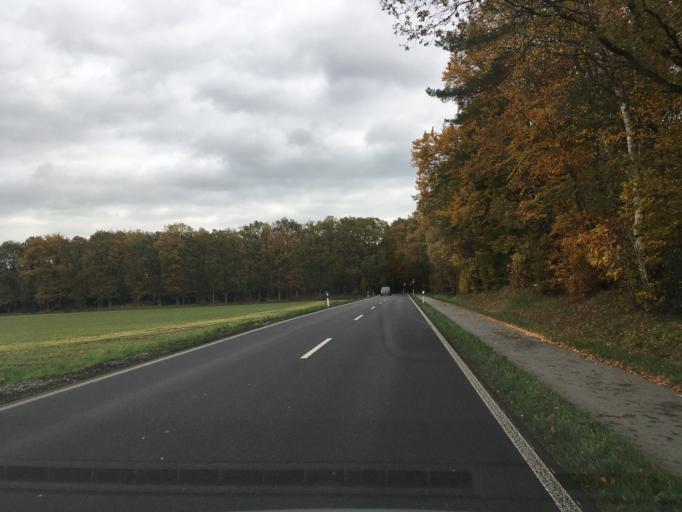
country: DE
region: North Rhine-Westphalia
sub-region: Regierungsbezirk Munster
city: Klein Reken
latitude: 51.8415
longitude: 7.0650
